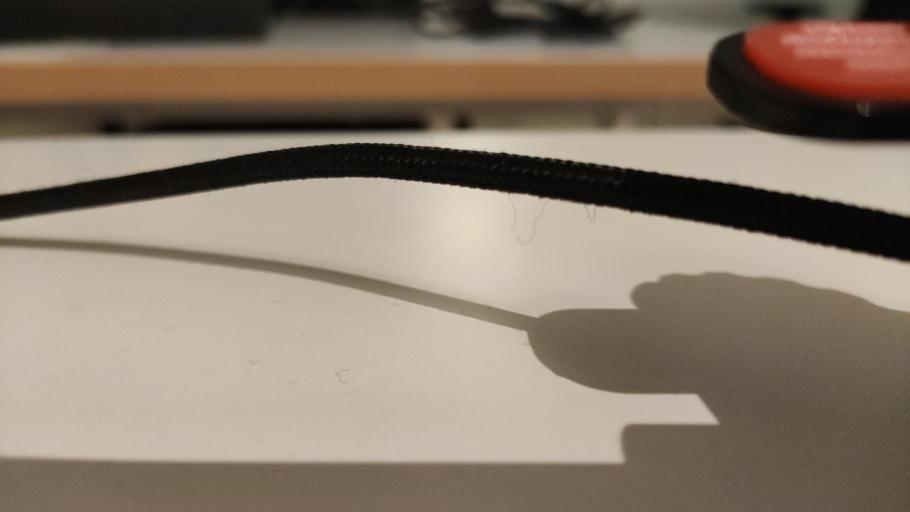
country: RU
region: Moskovskaya
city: Novosin'kovo
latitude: 56.3907
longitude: 37.2962
